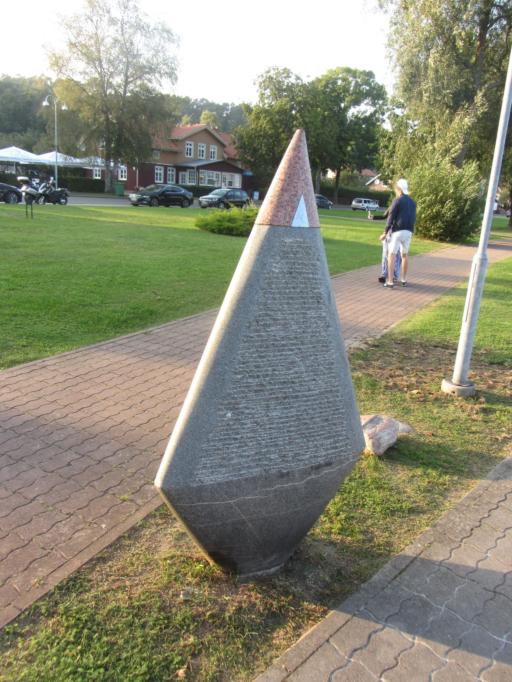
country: LT
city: Neringa
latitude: 55.5363
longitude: 21.1182
